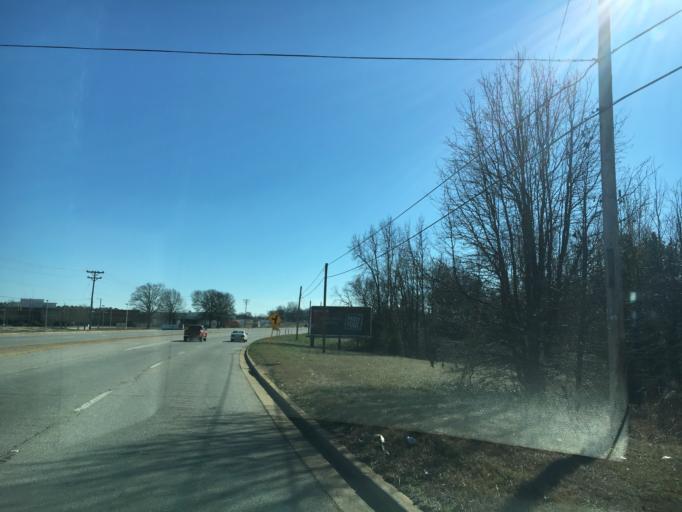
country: US
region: South Carolina
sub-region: Anderson County
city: Homeland Park
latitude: 34.4378
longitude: -82.6628
